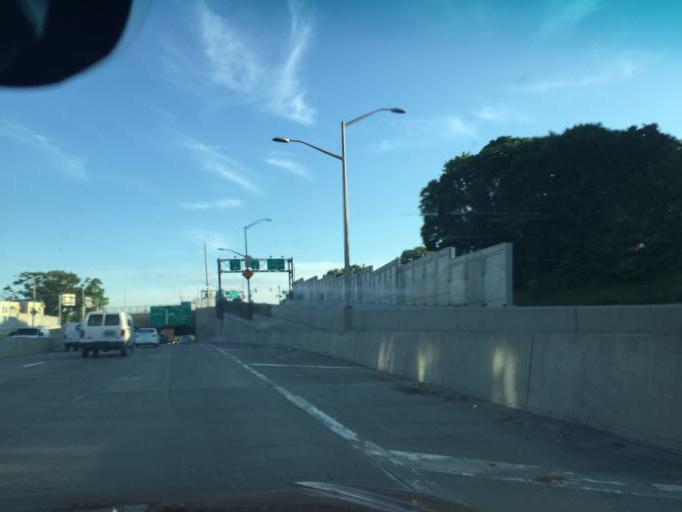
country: US
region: New York
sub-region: Queens County
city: Long Island City
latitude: 40.7471
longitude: -73.8951
